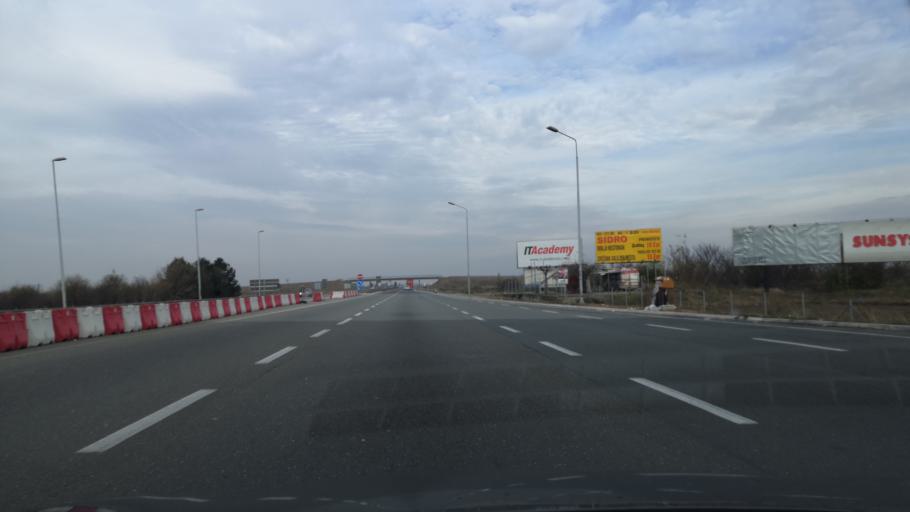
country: RS
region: Autonomna Pokrajina Vojvodina
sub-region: Sremski Okrug
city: Stara Pazova
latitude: 45.0072
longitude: 20.2012
